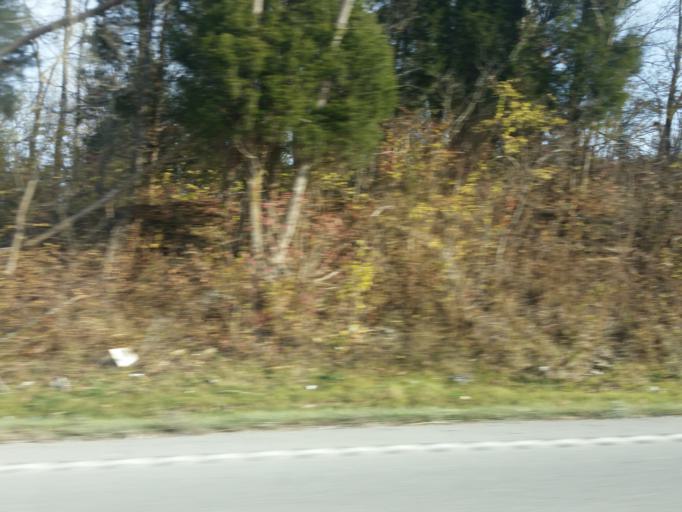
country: US
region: Kentucky
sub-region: Pendleton County
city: Falmouth
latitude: 38.7309
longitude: -84.3720
